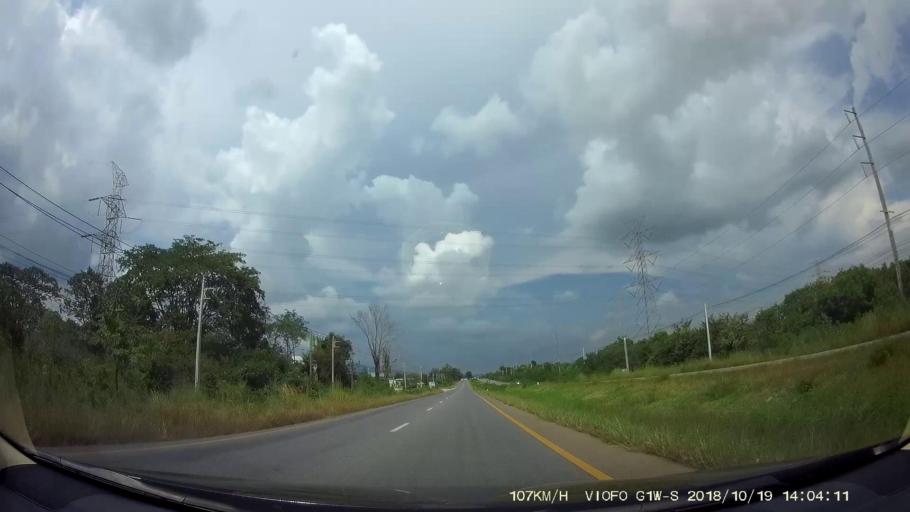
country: TH
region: Chaiyaphum
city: Chaiyaphum
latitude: 15.8605
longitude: 102.0785
